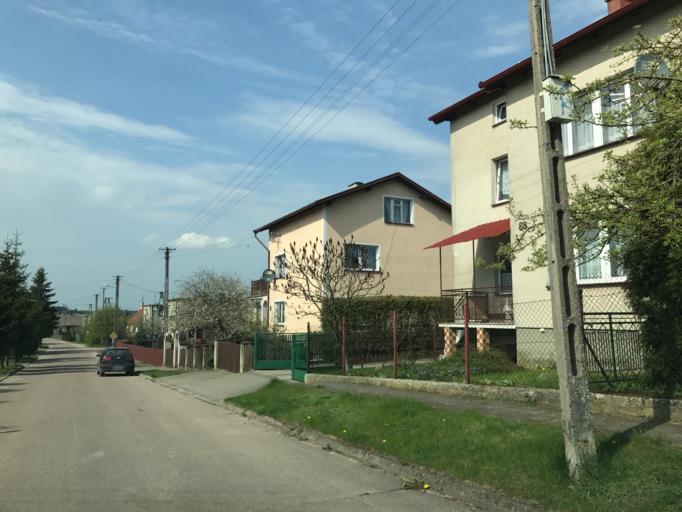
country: PL
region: Warmian-Masurian Voivodeship
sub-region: Powiat dzialdowski
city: Rybno
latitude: 53.3964
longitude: 19.8430
